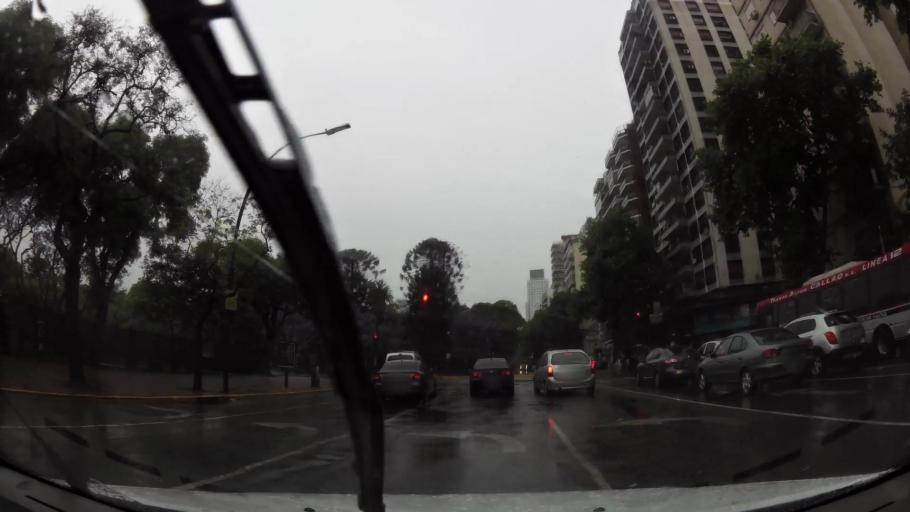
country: AR
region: Buenos Aires F.D.
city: Colegiales
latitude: -34.5816
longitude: -58.4210
